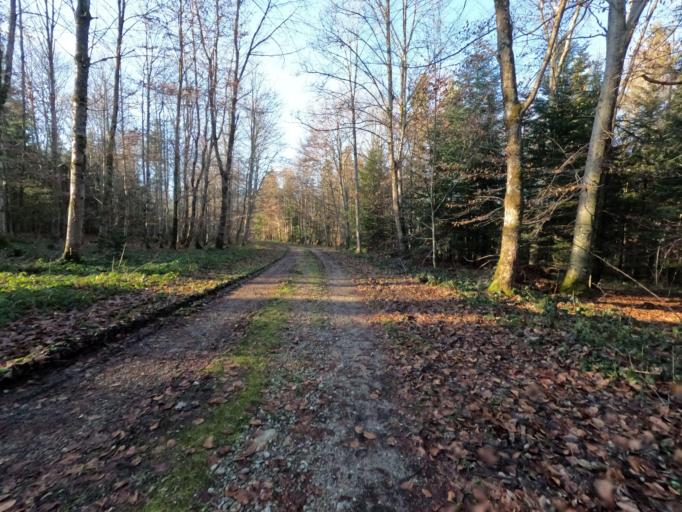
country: DE
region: Bavaria
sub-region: Upper Bavaria
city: Traunstein
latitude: 47.8958
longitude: 12.6269
